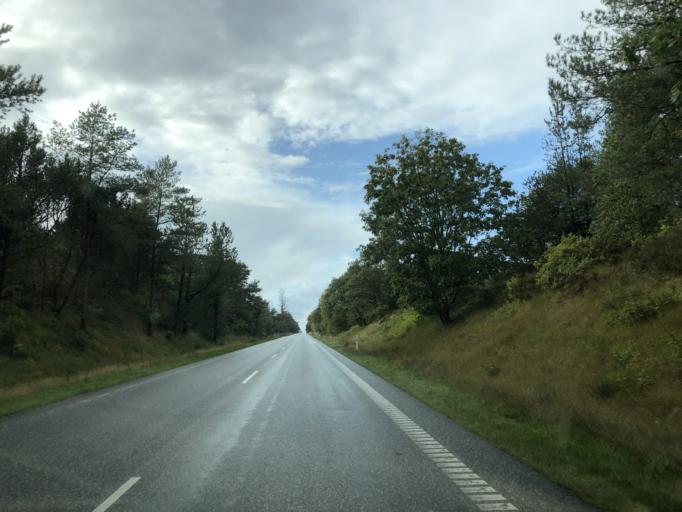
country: DK
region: North Denmark
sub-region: Vesthimmerland Kommune
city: Alestrup
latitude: 56.6111
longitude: 9.4224
